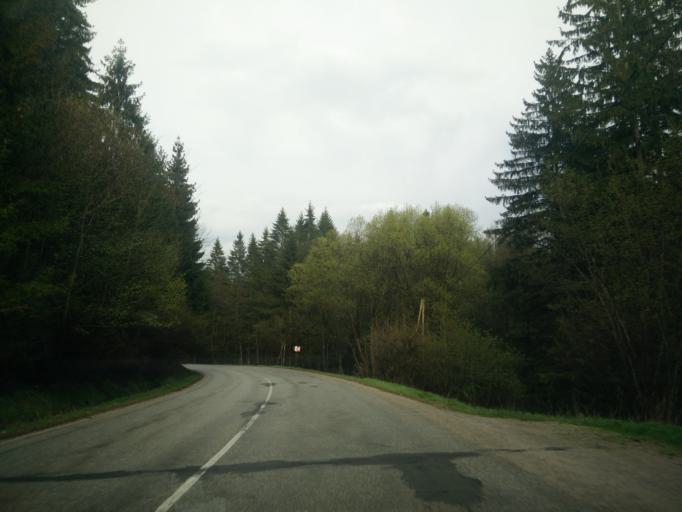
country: SK
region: Banskobystricky
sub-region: Okres Ziar nad Hronom
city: Kremnica
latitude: 48.8371
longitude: 18.9134
